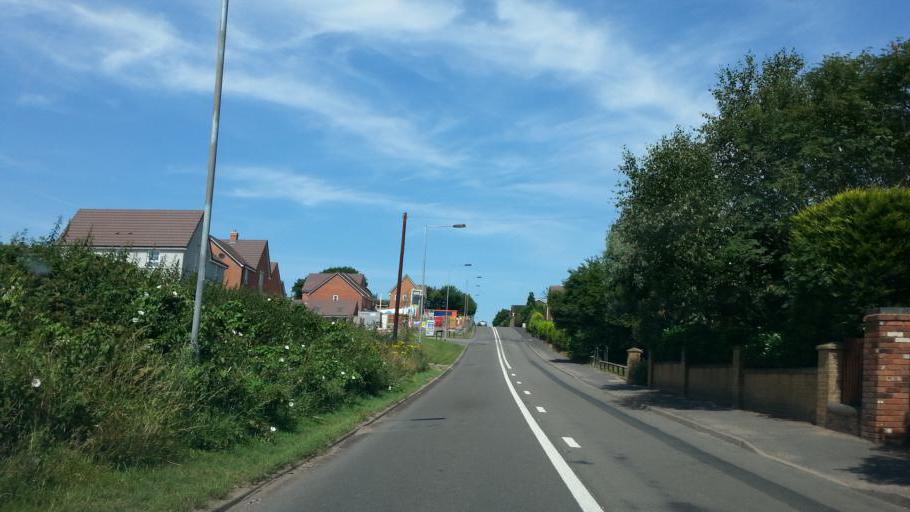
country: GB
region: England
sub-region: Staffordshire
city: Cannock
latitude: 52.7182
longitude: -2.0216
